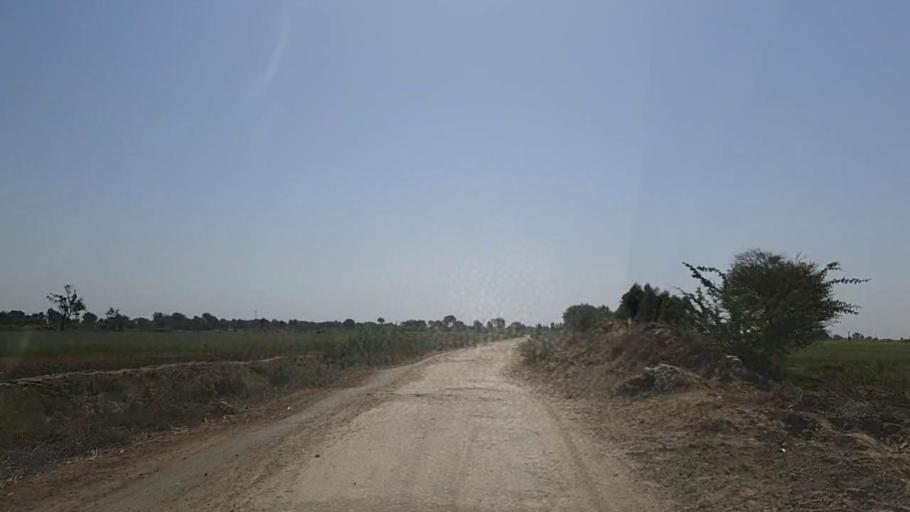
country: PK
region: Sindh
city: Samaro
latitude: 25.2473
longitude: 69.4106
